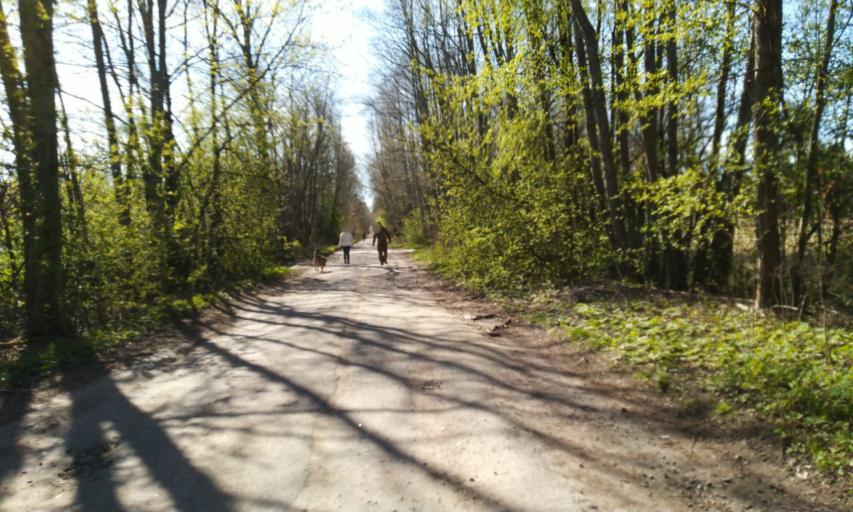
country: RU
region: Leningrad
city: Garbolovo
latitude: 60.3885
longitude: 30.4823
